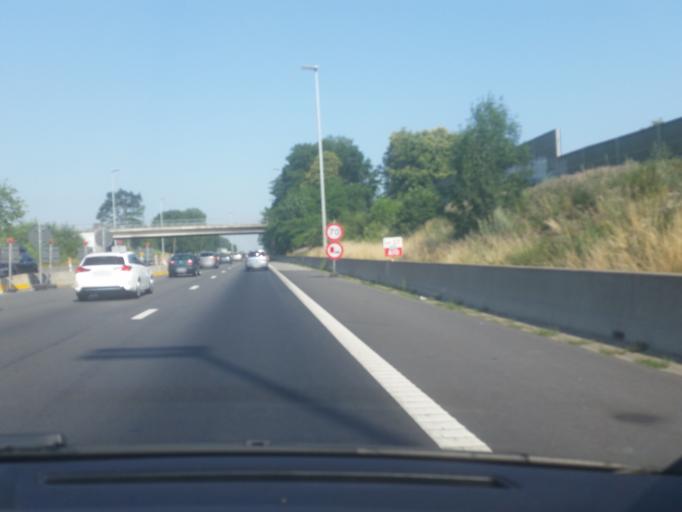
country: BE
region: Flanders
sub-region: Provincie Oost-Vlaanderen
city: Herzele
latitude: 50.9345
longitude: 3.9302
